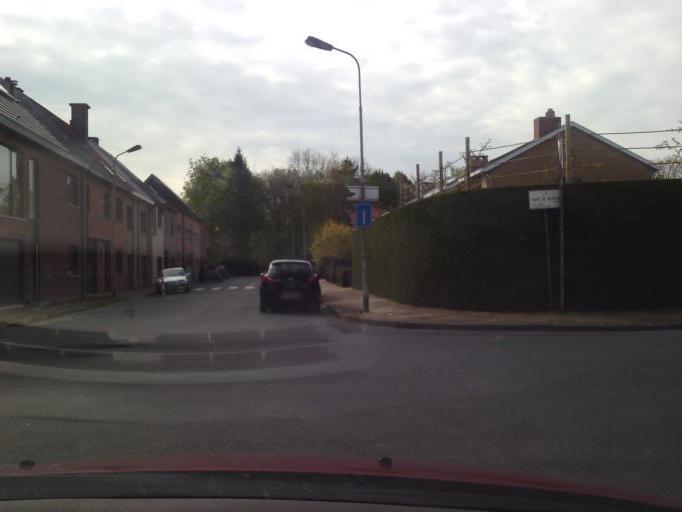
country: BE
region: Flanders
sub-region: Provincie Oost-Vlaanderen
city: Gent
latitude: 51.0577
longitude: 3.6900
